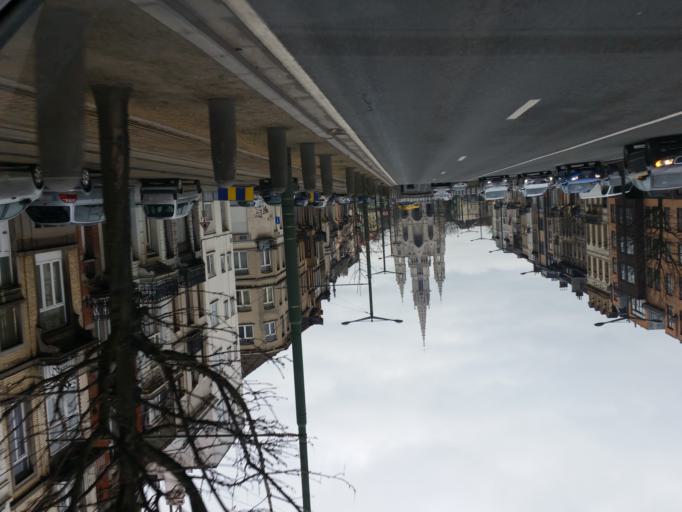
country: BE
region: Brussels Capital
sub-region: Bruxelles-Capitale
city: Brussels
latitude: 50.8747
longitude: 4.3587
